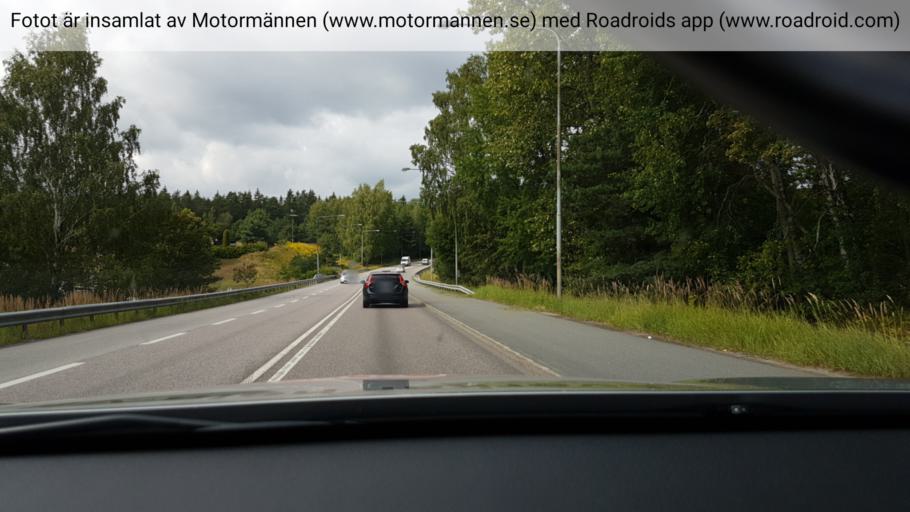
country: SE
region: Stockholm
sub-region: Tyreso Kommun
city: Bollmora
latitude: 59.2299
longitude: 18.1984
